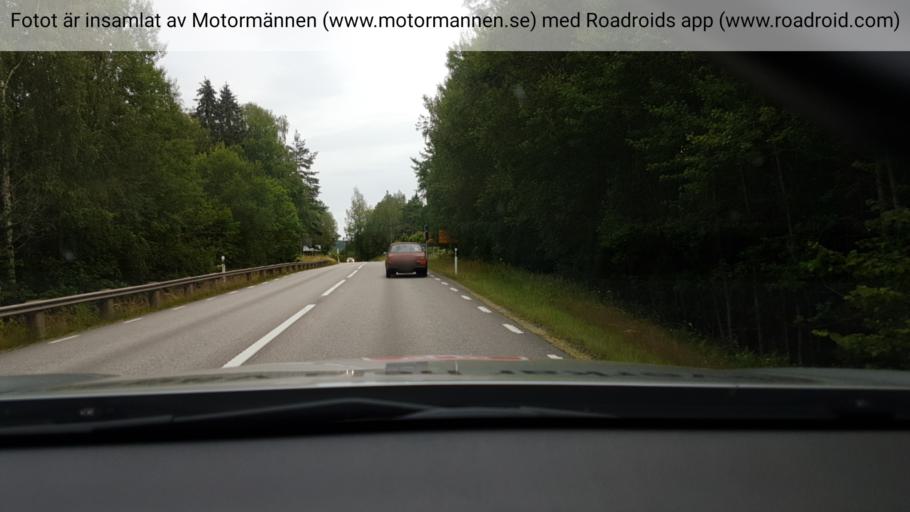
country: SE
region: Vaestra Goetaland
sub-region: Bengtsfors Kommun
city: Billingsfors
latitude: 58.9259
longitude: 12.2153
